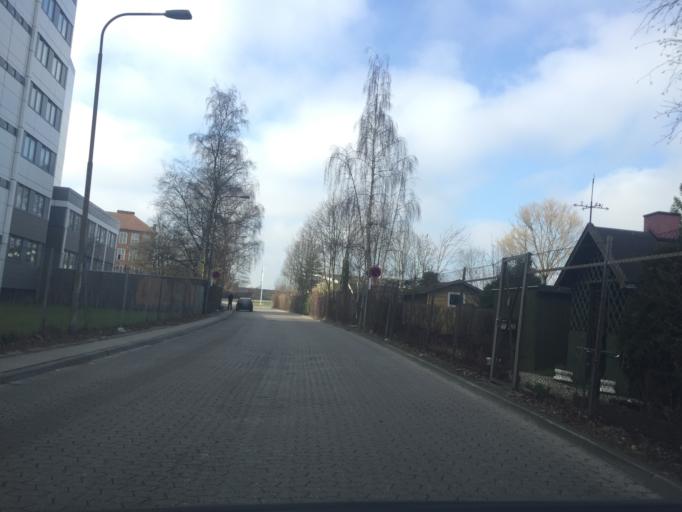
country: DK
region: Capital Region
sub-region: Kobenhavn
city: Copenhagen
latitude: 55.7164
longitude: 12.5717
